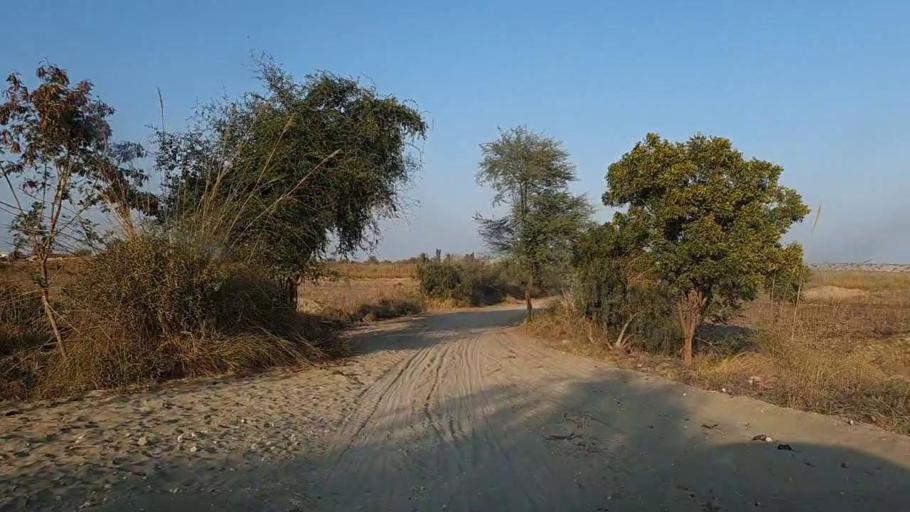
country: PK
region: Sindh
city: Sanghar
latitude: 26.2950
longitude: 68.9846
